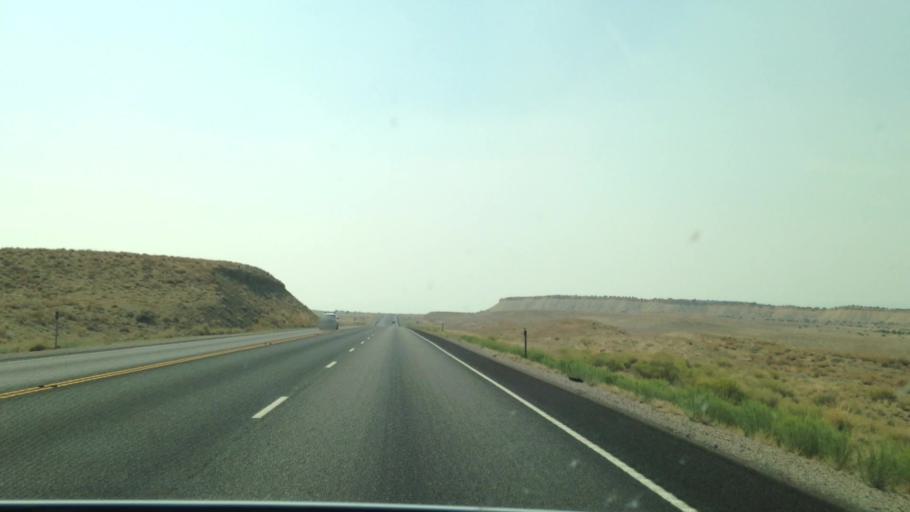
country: US
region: Utah
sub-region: Carbon County
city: Wellington
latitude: 39.5379
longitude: -110.6050
